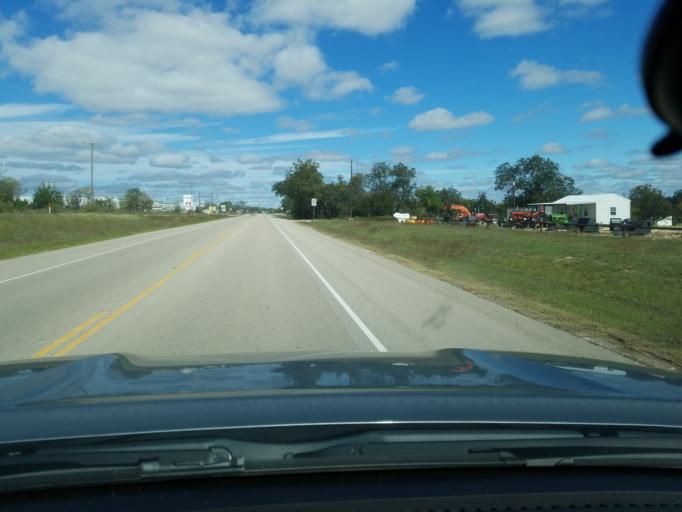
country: US
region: Texas
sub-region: Hamilton County
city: Hamilton
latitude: 31.6879
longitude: -98.1306
